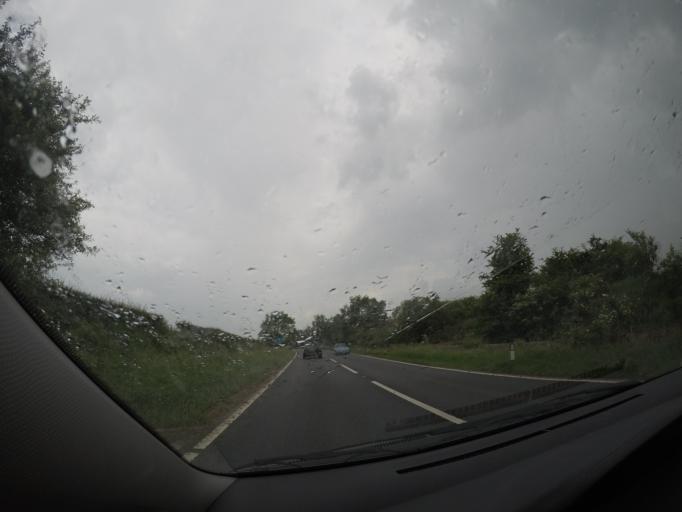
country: GB
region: England
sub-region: Cumbria
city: Appleby-in-Westmorland
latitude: 54.6116
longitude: -2.5457
